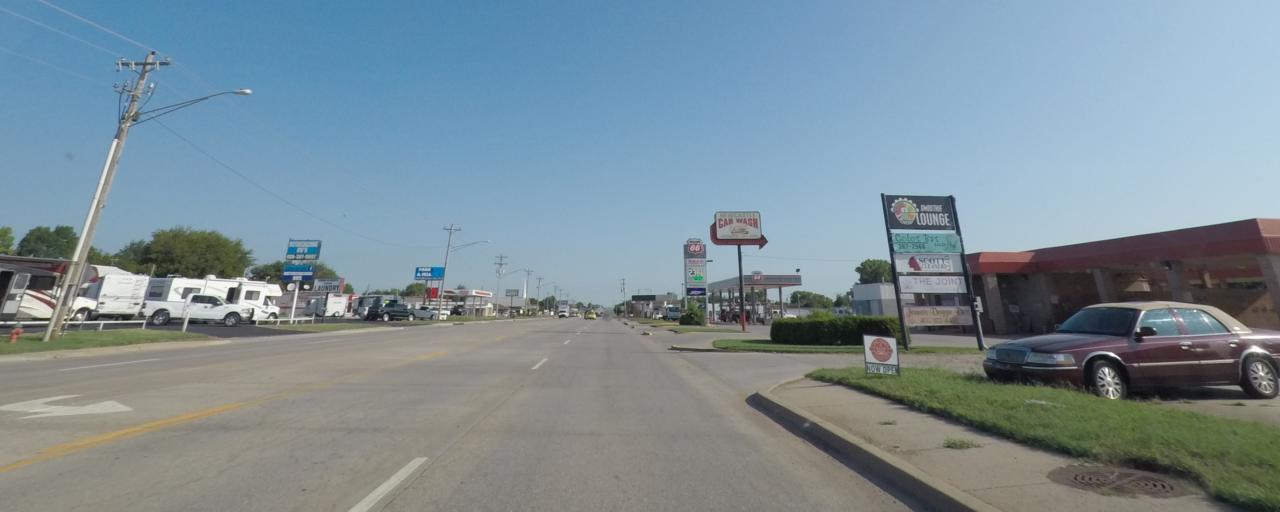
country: US
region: Oklahoma
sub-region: McClain County
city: Newcastle
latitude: 35.2571
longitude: -97.6001
